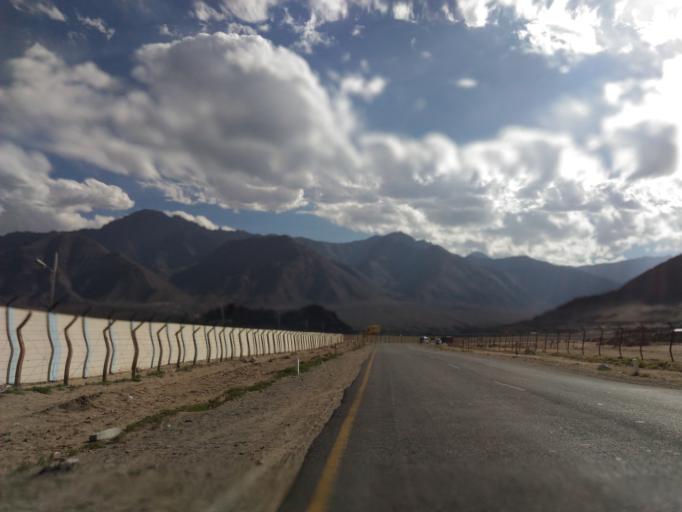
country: IN
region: Kashmir
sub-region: Ladakh
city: Leh
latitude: 34.1355
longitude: 77.5348
